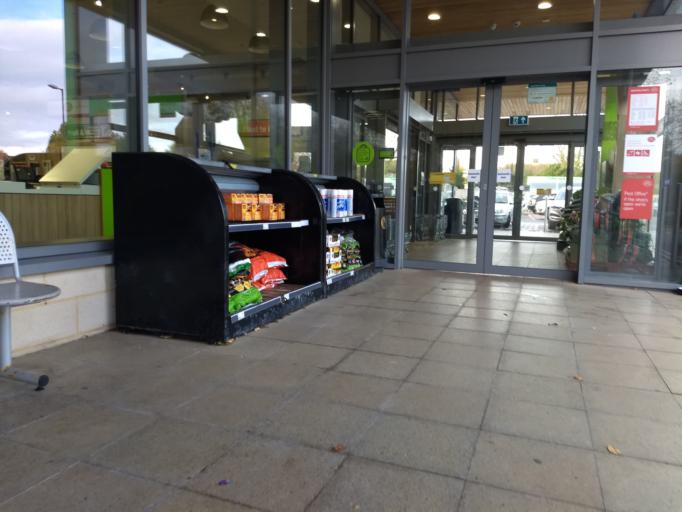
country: GB
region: England
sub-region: Isle of Wight
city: Freshwater
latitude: 50.6806
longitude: -1.5149
